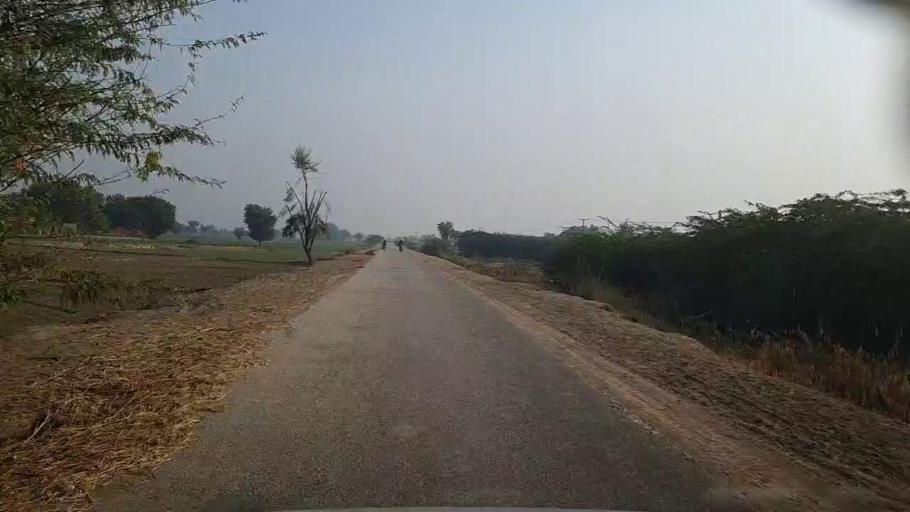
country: PK
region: Sindh
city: Kandiari
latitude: 27.0517
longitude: 68.4666
